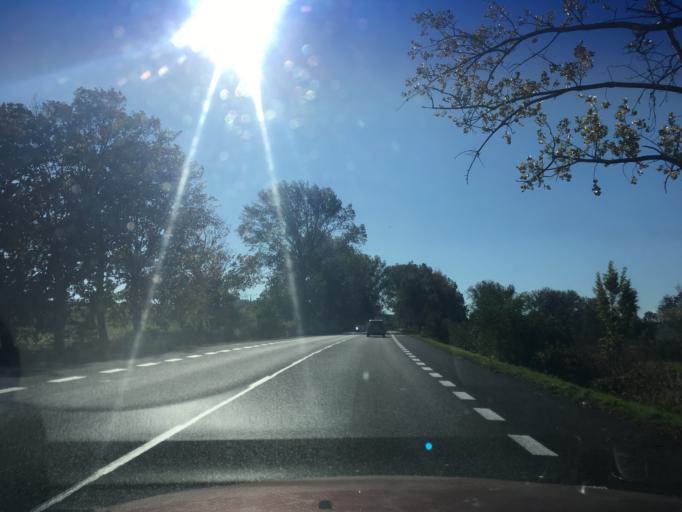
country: DE
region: Saxony
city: Ostritz
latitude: 51.0038
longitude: 14.9486
